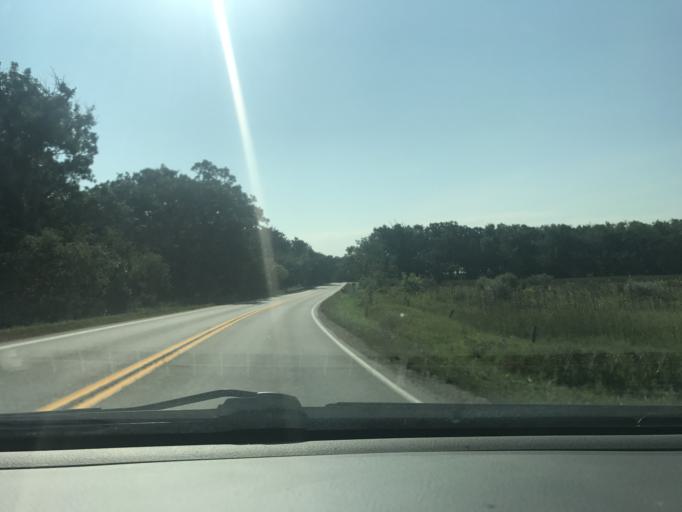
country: US
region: Illinois
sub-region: Kane County
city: Pingree Grove
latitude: 42.0691
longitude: -88.4359
